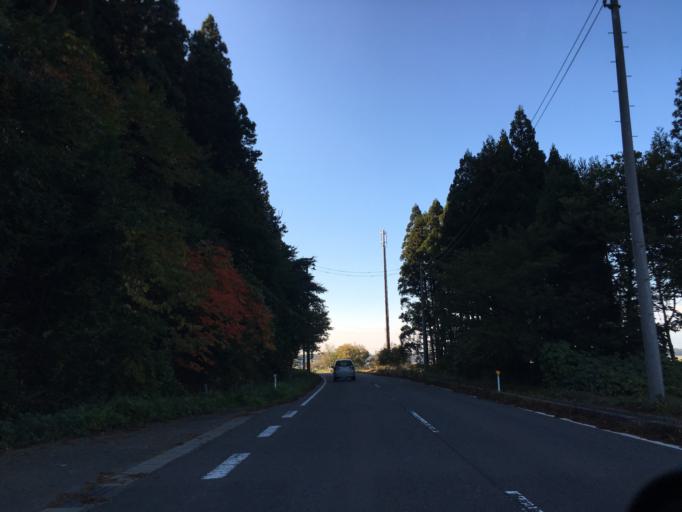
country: JP
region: Fukushima
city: Inawashiro
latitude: 37.4138
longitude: 140.1422
